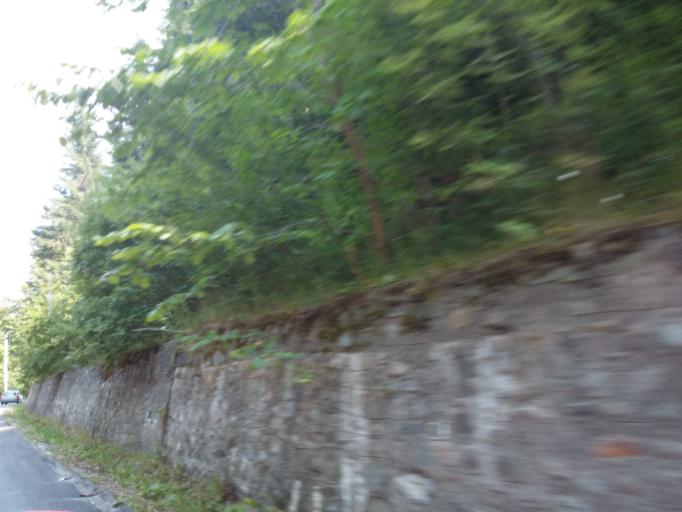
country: RO
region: Valcea
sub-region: Comuna Voineasa
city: Voineasa
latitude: 45.4339
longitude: 23.8573
